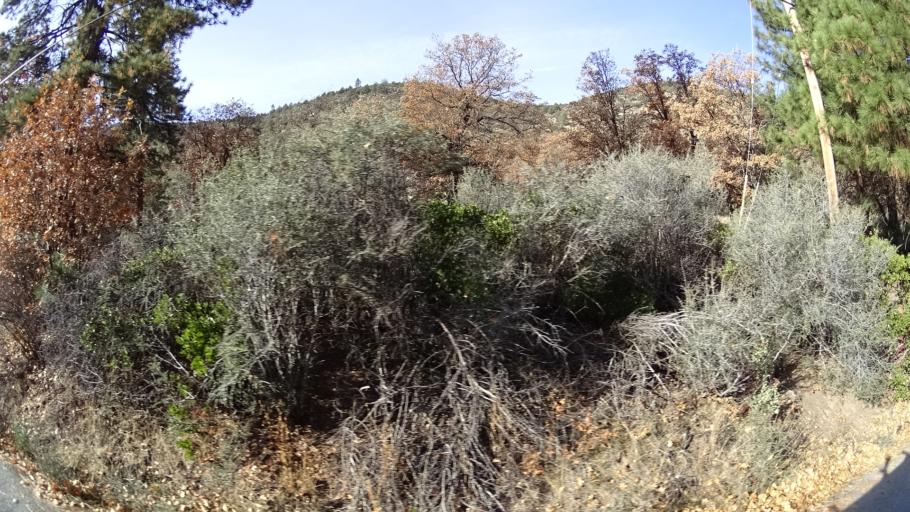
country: US
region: California
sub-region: Siskiyou County
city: Montague
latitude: 41.6129
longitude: -122.5778
